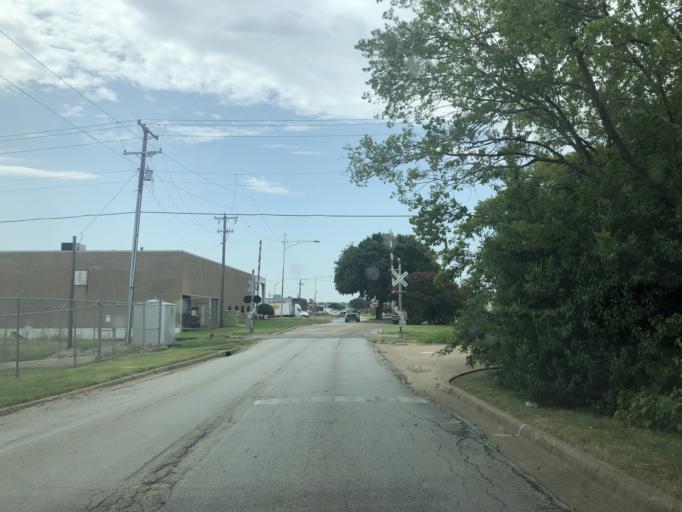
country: US
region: Texas
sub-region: Dallas County
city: Grand Prairie
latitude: 32.7580
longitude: -97.0457
